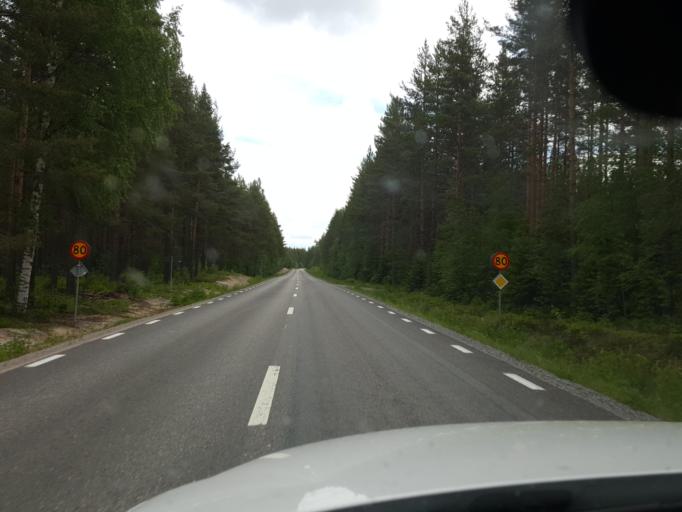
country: SE
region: Gaevleborg
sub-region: Ljusdals Kommun
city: Farila
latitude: 61.7962
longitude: 15.6767
